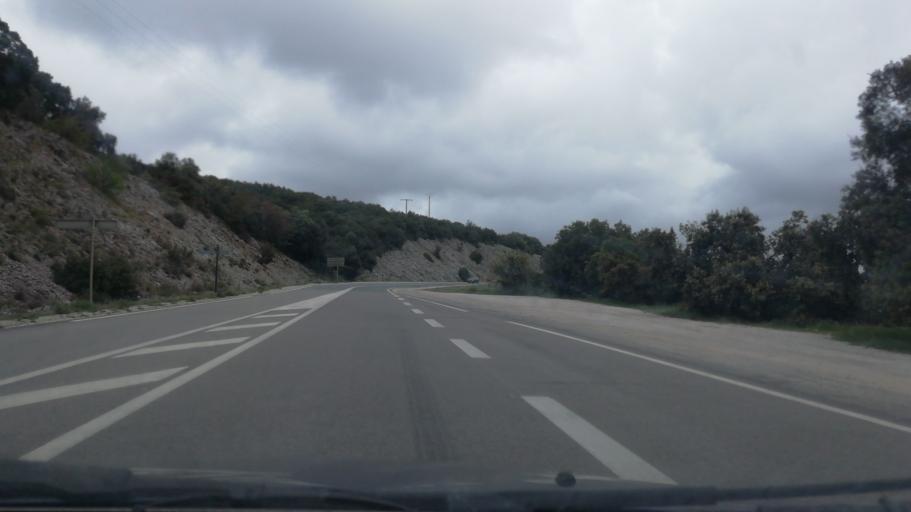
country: FR
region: Languedoc-Roussillon
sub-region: Departement de l'Herault
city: Les Matelles
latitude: 43.7251
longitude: 3.7947
